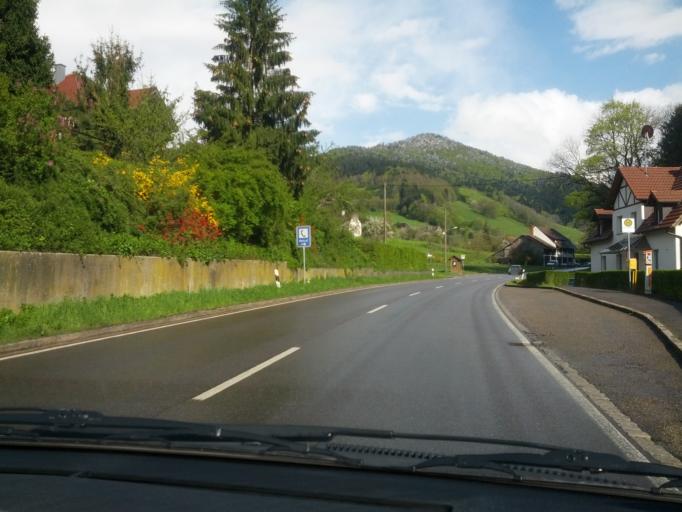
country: DE
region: Baden-Wuerttemberg
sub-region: Freiburg Region
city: Glottertal
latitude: 48.0444
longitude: 7.9752
